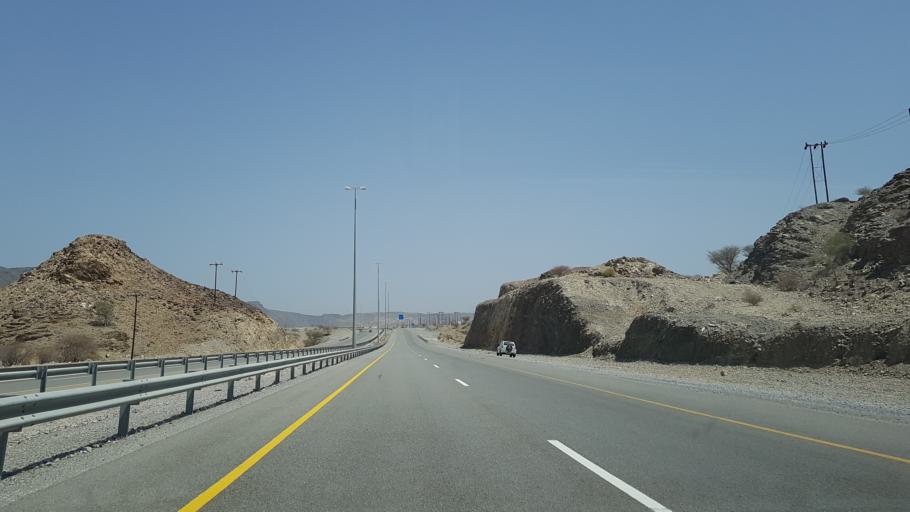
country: OM
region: Muhafazat Masqat
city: Muscat
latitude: 23.2514
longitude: 58.7821
